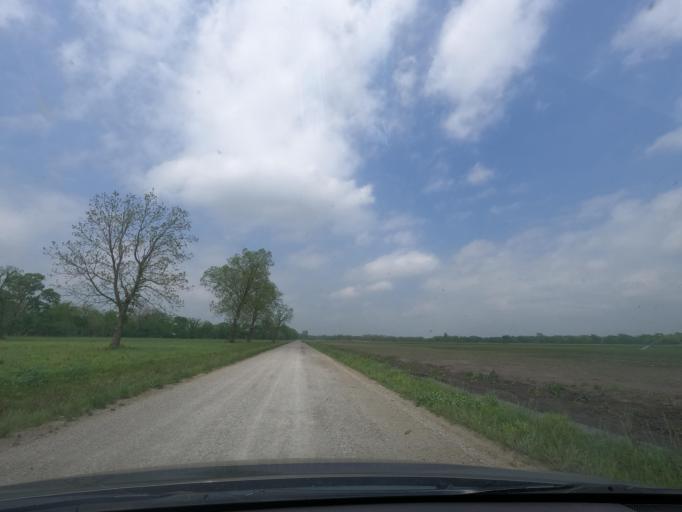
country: US
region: Kansas
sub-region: Labette County
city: Oswego
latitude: 37.2828
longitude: -95.0134
